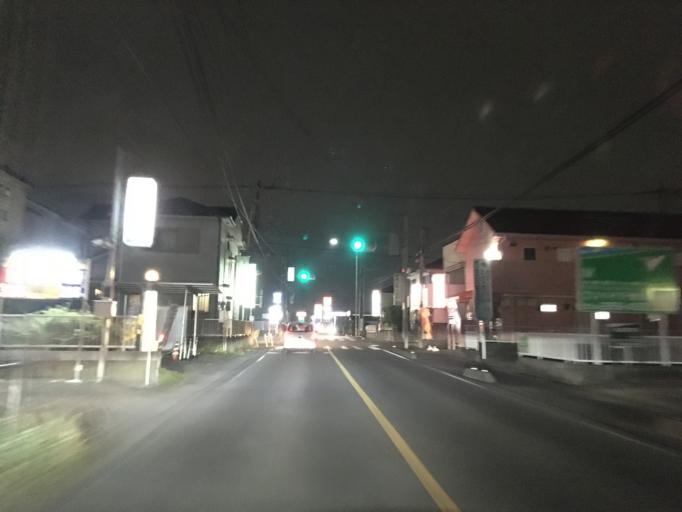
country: JP
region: Saitama
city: Sayama
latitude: 35.8271
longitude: 139.4354
